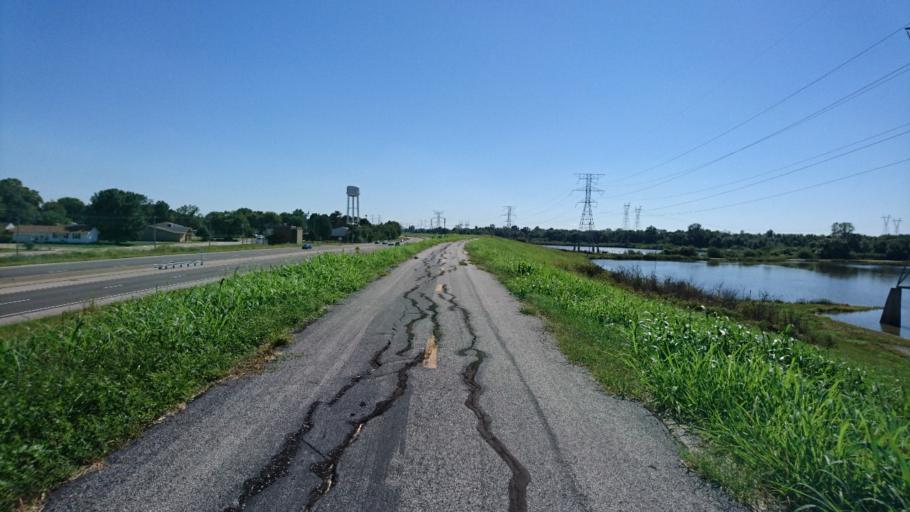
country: US
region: Illinois
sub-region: Madison County
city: Hartford
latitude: 38.8359
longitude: -90.0987
